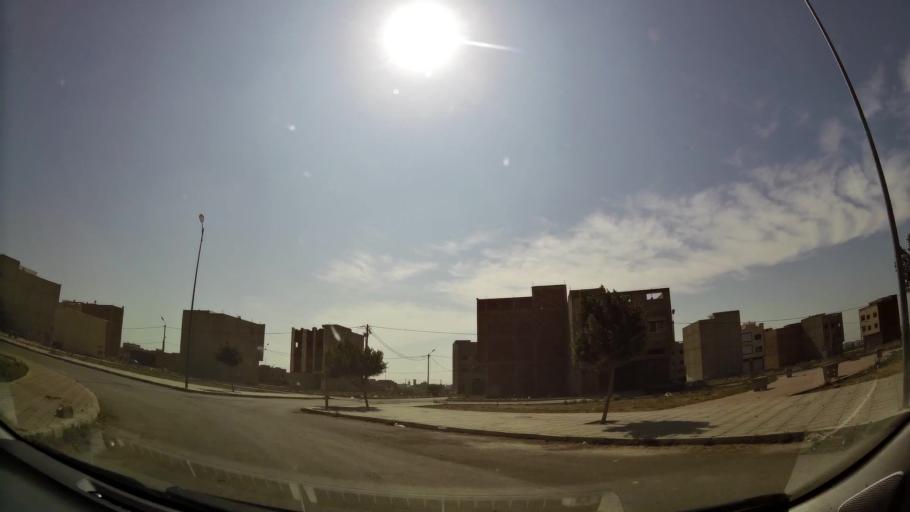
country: MA
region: Oriental
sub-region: Oujda-Angad
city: Oujda
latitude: 34.6980
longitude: -1.8691
